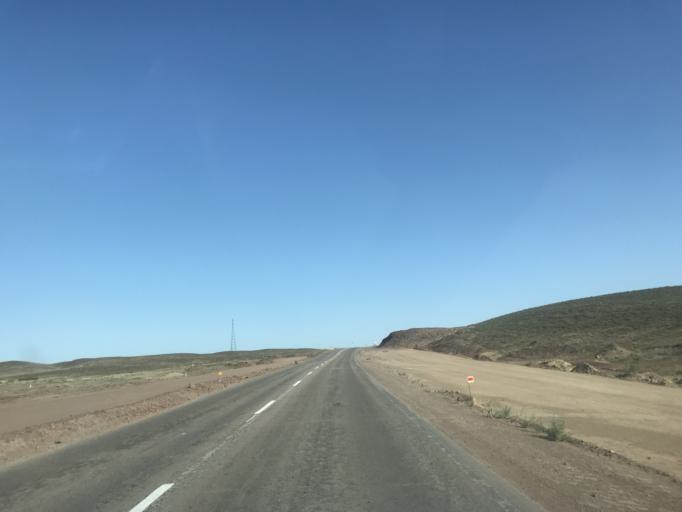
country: KZ
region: Zhambyl
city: Mynaral
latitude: 45.3335
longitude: 73.7225
